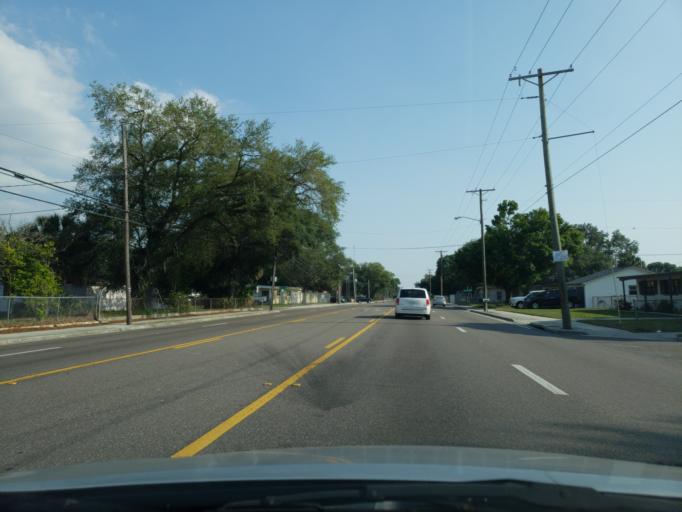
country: US
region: Florida
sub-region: Hillsborough County
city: Palm River-Clair Mel
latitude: 27.9290
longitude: -82.3687
